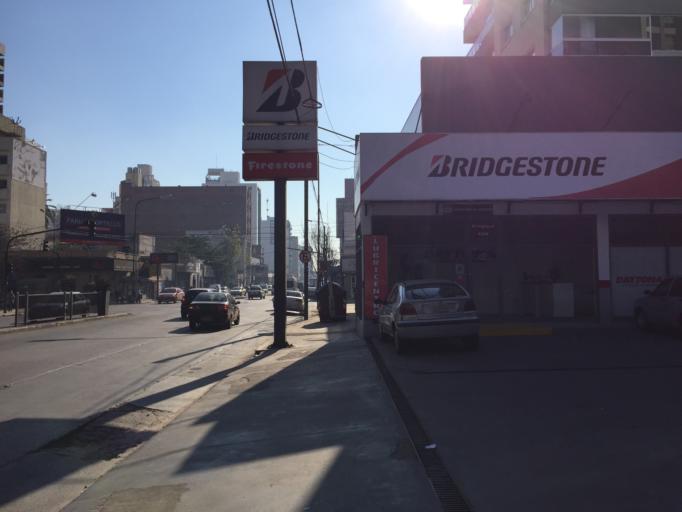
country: AR
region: Buenos Aires
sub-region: Partido de Lomas de Zamora
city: Lomas de Zamora
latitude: -34.7645
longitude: -58.4034
